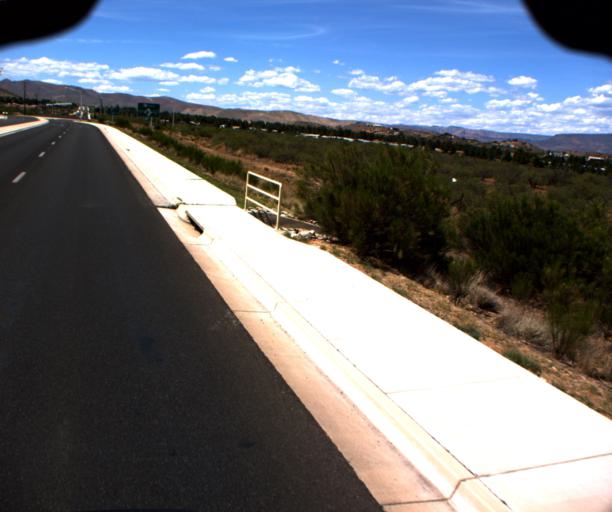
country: US
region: Arizona
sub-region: Yavapai County
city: Clarkdale
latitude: 34.7455
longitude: -112.0431
